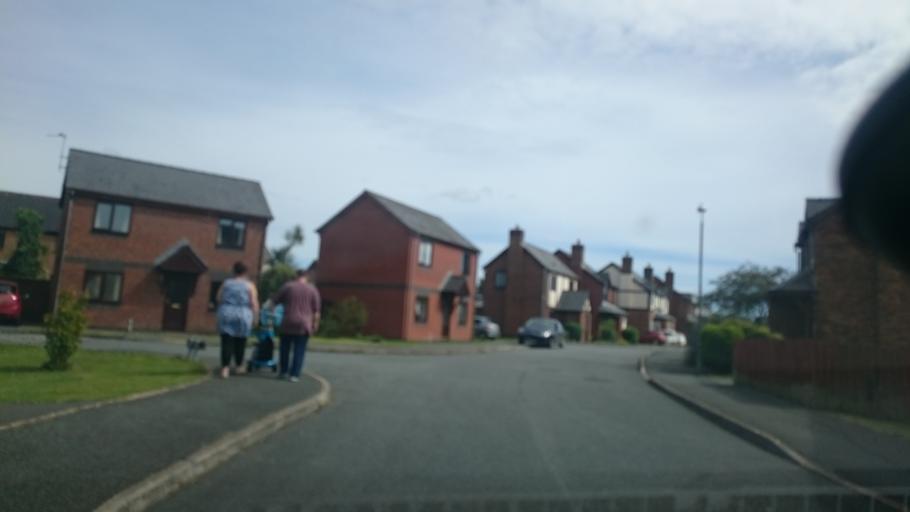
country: GB
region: Wales
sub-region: Pembrokeshire
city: Haverfordwest
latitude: 51.7871
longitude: -4.9713
